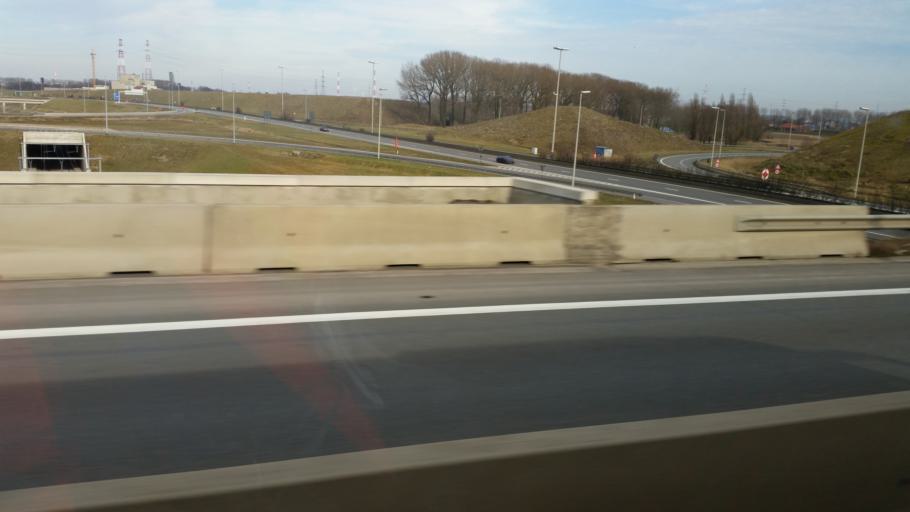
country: BE
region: Flanders
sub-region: Provincie Oost-Vlaanderen
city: Beveren
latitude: 51.2509
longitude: 4.2579
